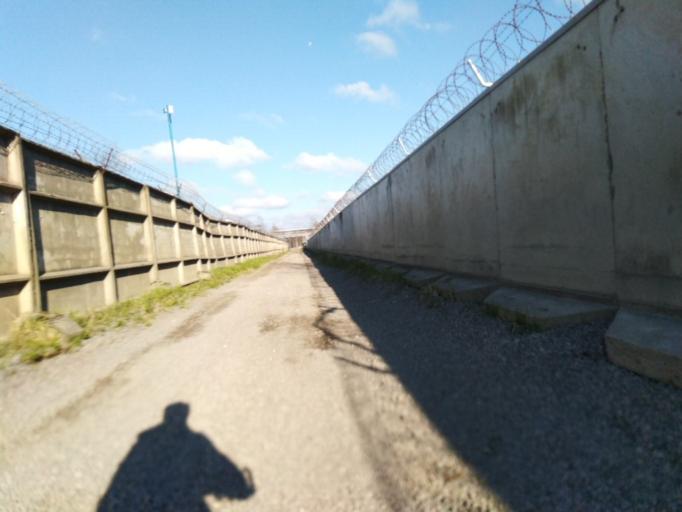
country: RU
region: Leningrad
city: Novoye Devyatkino
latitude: 60.0723
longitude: 30.4741
